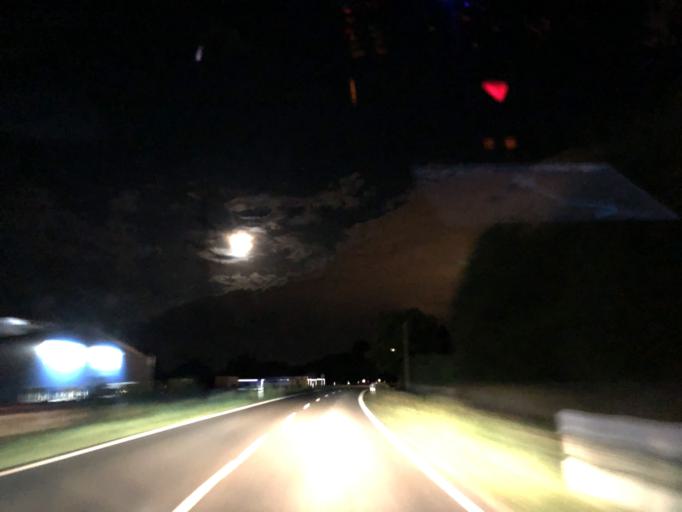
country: DE
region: Bavaria
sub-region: Upper Bavaria
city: Finsing
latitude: 48.2281
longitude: 11.8127
